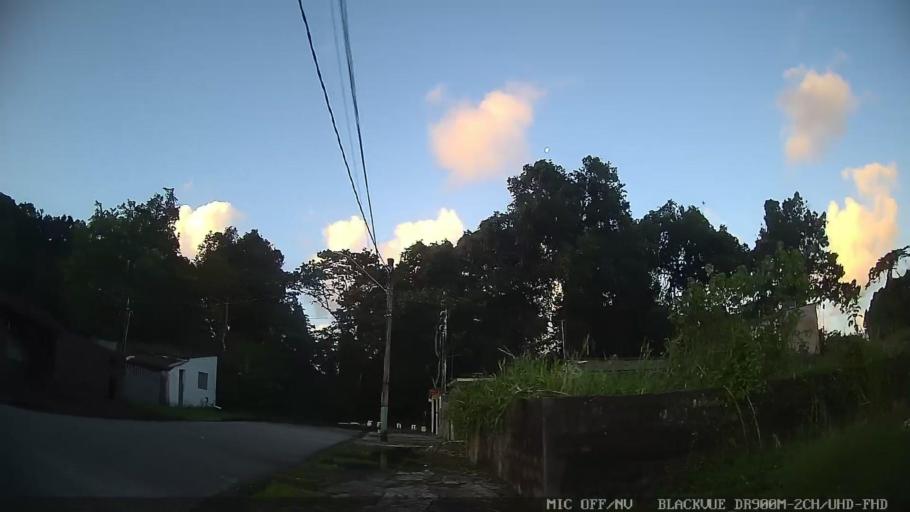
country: BR
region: Sao Paulo
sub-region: Itanhaem
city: Itanhaem
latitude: -24.1432
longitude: -46.7337
